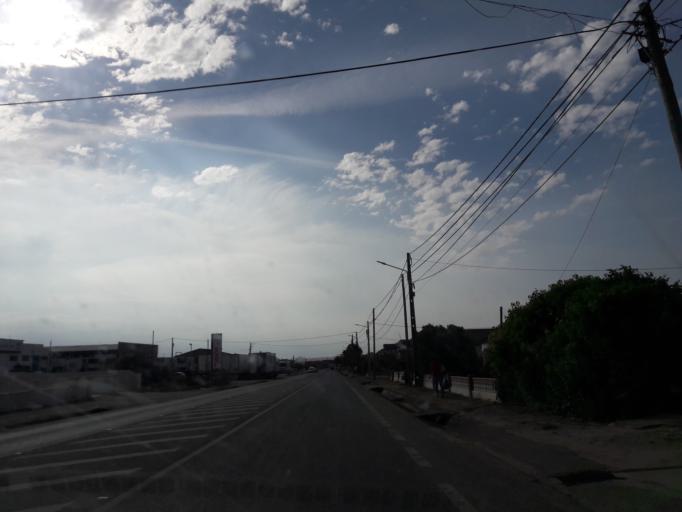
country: PT
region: Leiria
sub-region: Peniche
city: Atouguia da Baleia
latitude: 39.3413
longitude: -9.3321
